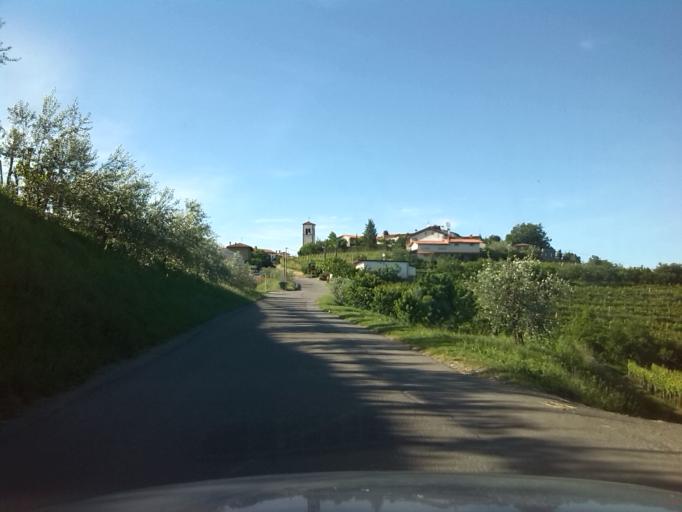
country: SI
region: Brda
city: Dobrovo
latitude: 45.9880
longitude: 13.5203
